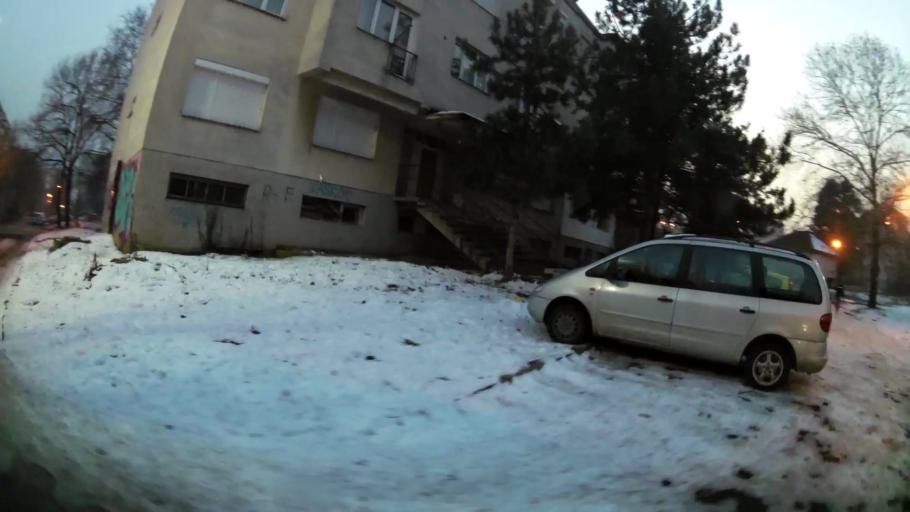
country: MK
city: Creshevo
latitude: 42.0109
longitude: 21.5099
